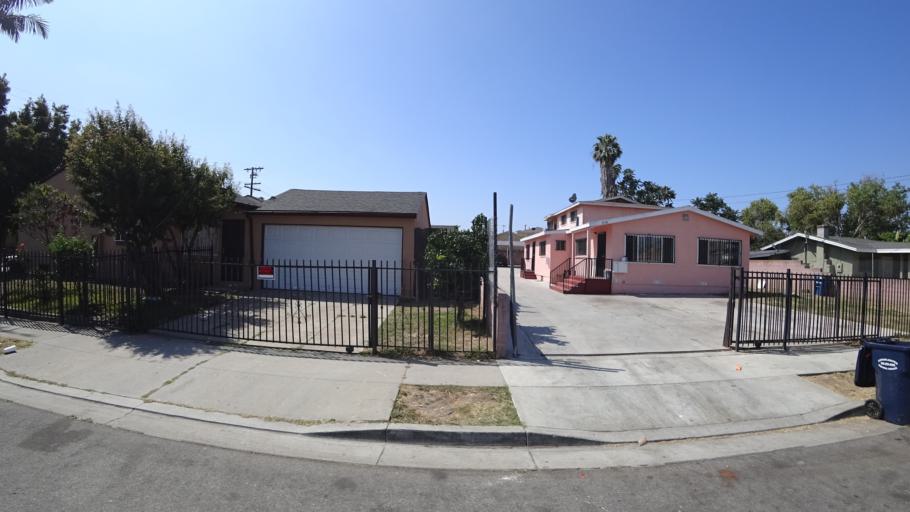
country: US
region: California
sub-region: Los Angeles County
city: Westmont
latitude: 33.9373
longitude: -118.2966
